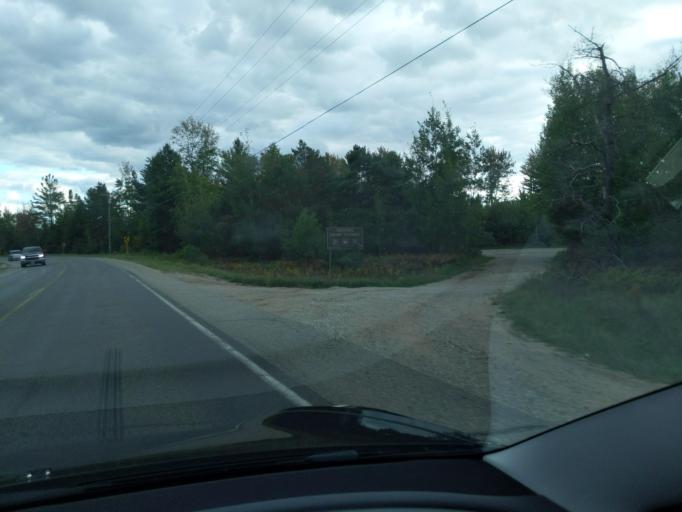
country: US
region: Michigan
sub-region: Kalkaska County
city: Rapid City
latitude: 44.8113
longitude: -85.2828
